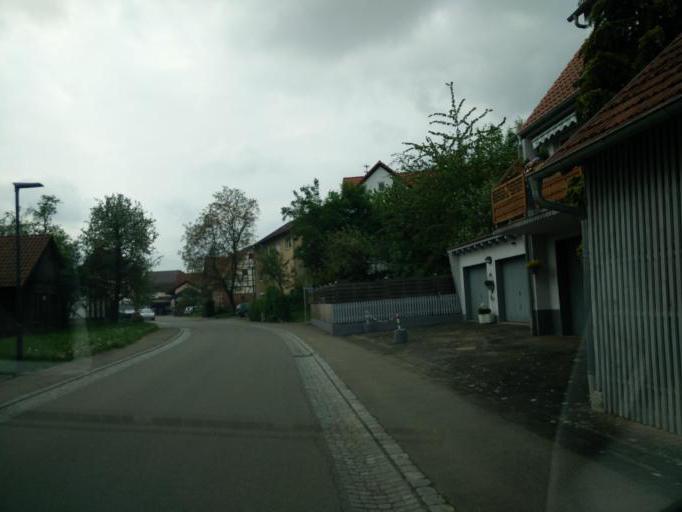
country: DE
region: Baden-Wuerttemberg
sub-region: Tuebingen Region
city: Gomaringen
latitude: 48.4867
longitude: 9.1115
